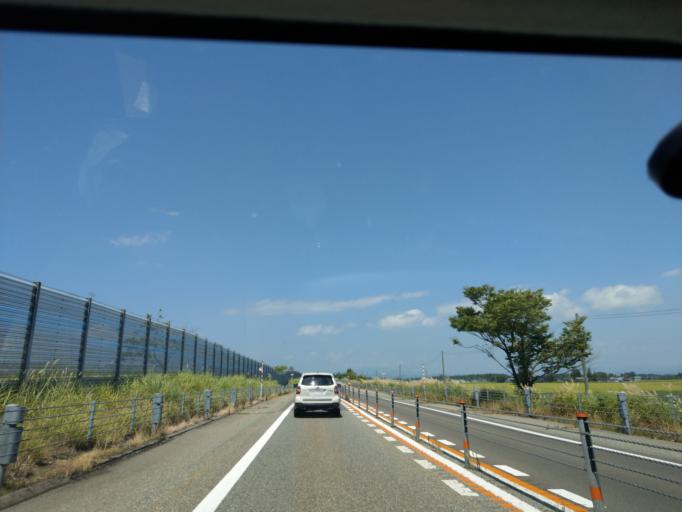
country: JP
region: Akita
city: Omagari
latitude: 39.3857
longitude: 140.4789
